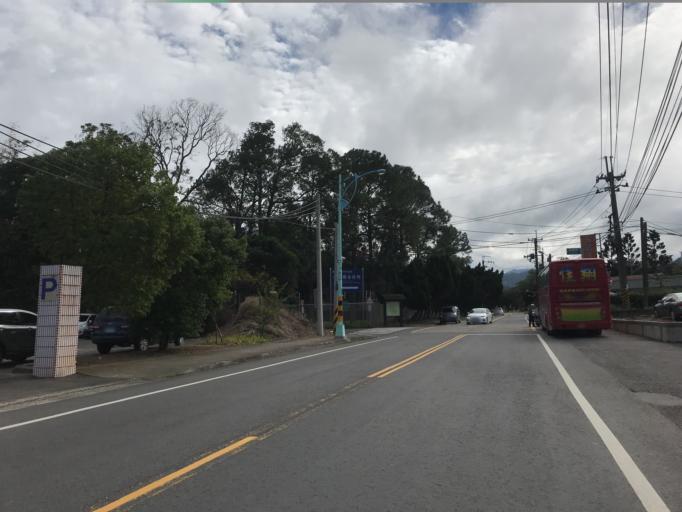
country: TW
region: Taiwan
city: Daxi
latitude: 24.8383
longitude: 121.2404
